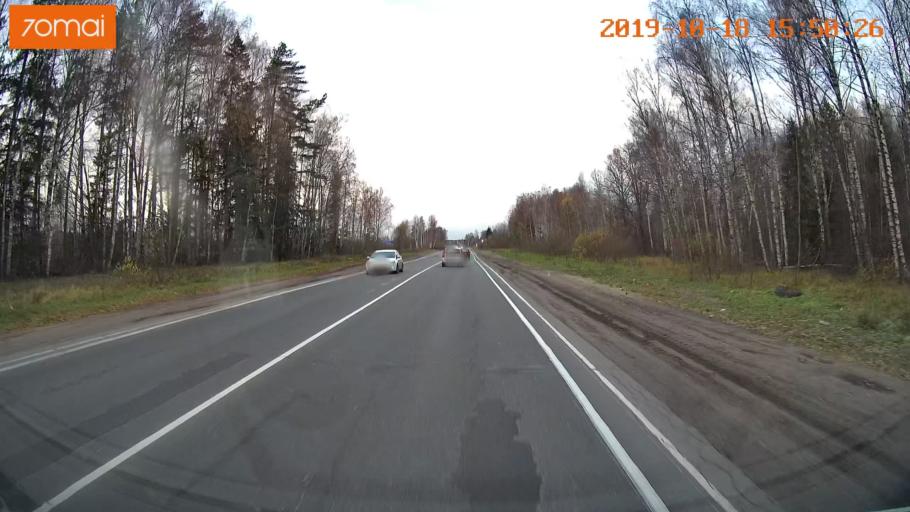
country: RU
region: Vladimir
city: Kommunar
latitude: 56.0324
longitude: 40.5600
